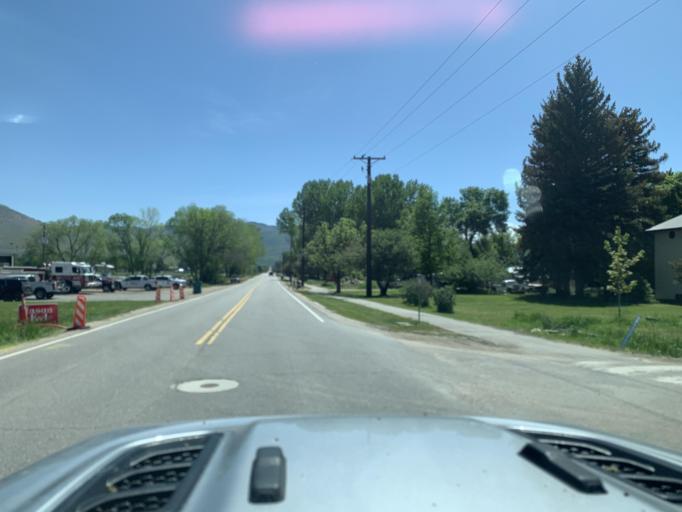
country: US
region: Utah
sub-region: Weber County
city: Wolf Creek
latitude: 41.2933
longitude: -111.8063
